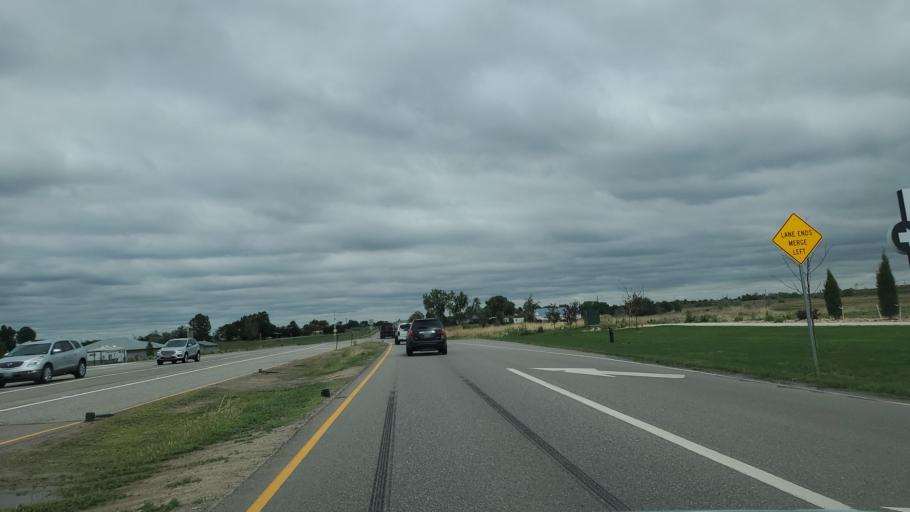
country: US
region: Colorado
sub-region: Adams County
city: Brighton
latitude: 39.9143
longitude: -104.8335
